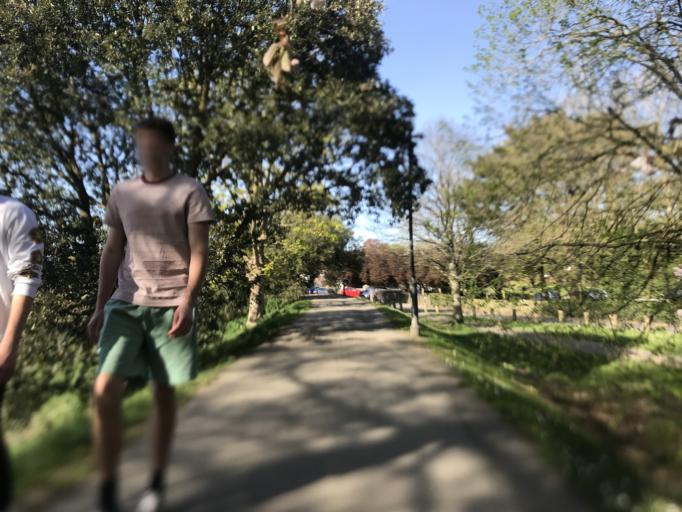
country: GB
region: England
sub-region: Devon
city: Barnstaple
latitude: 51.0708
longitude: -4.0543
